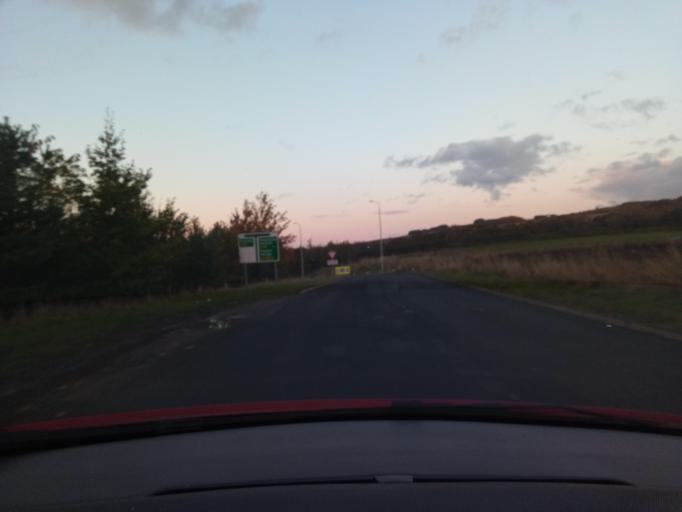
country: GB
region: England
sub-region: Northumberland
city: Warden
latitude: 54.9718
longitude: -2.2371
